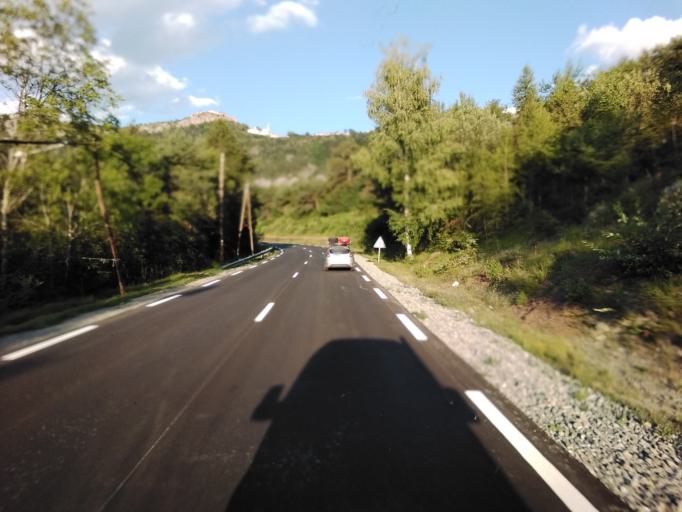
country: FR
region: Provence-Alpes-Cote d'Azur
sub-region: Departement des Alpes-de-Haute-Provence
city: Seyne-les-Alpes
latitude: 44.4469
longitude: 6.3612
